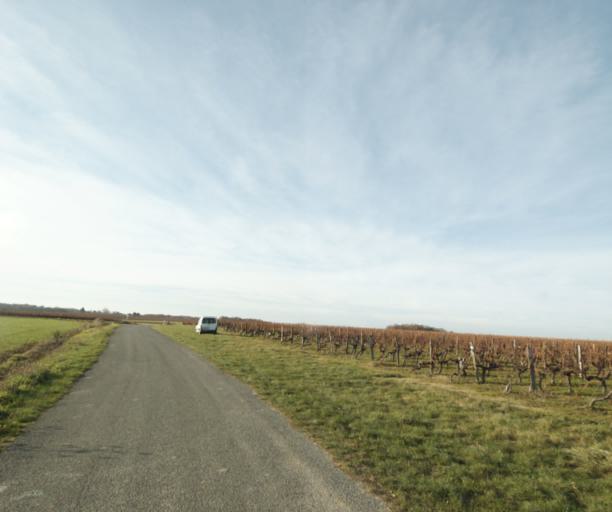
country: FR
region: Poitou-Charentes
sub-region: Departement de la Charente-Maritime
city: Chaniers
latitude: 45.7410
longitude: -0.5199
